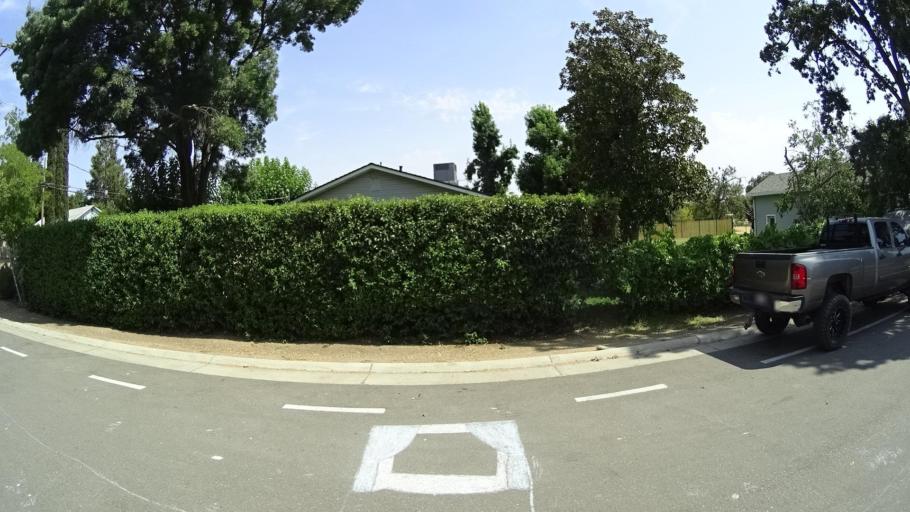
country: US
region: California
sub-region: Placer County
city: Rocklin
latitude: 38.7943
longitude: -121.2366
